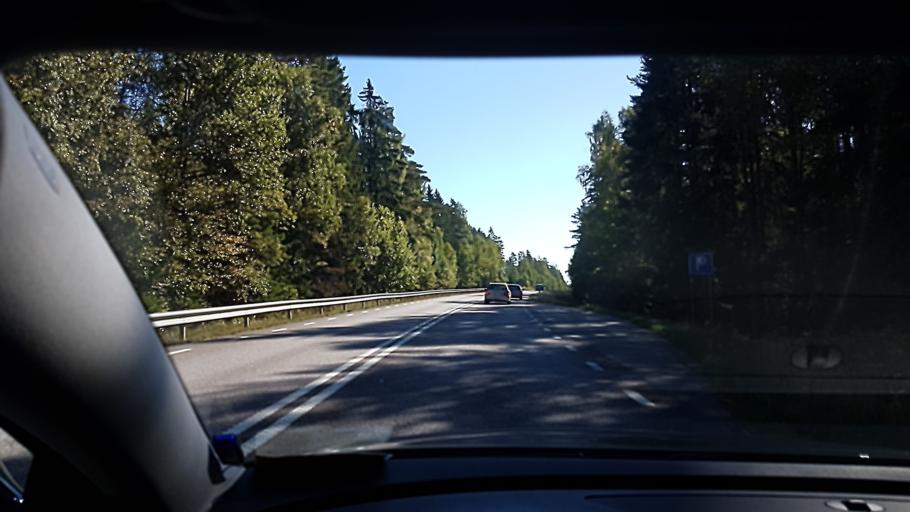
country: SE
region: Kronoberg
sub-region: Lessebo Kommun
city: Hovmantorp
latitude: 56.7866
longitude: 15.1842
